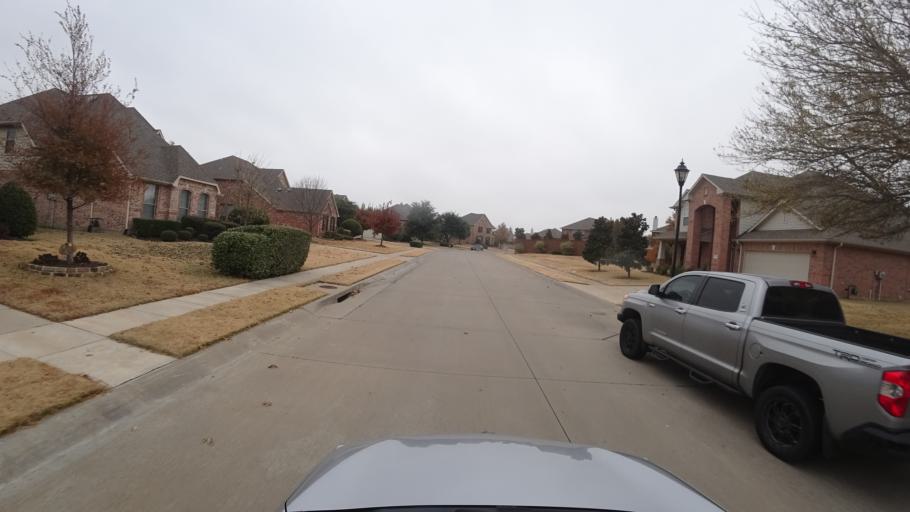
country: US
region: Texas
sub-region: Denton County
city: The Colony
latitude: 33.0687
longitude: -96.9030
